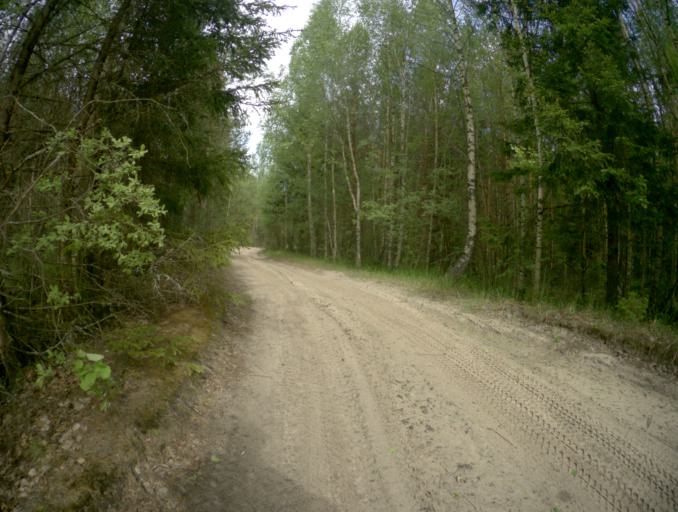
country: RU
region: Vladimir
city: Ivanishchi
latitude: 55.7493
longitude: 40.3789
